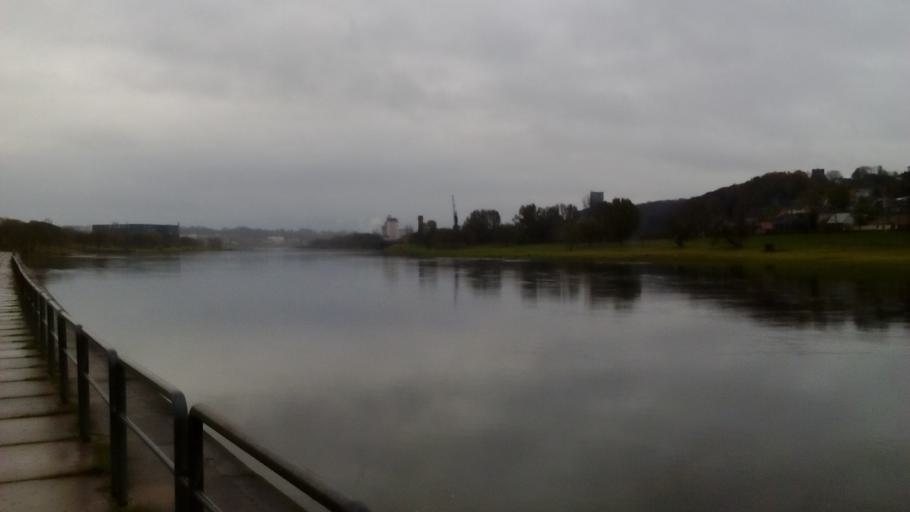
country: LT
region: Kauno apskritis
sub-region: Kaunas
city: Kaunas
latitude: 54.8946
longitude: 23.8932
